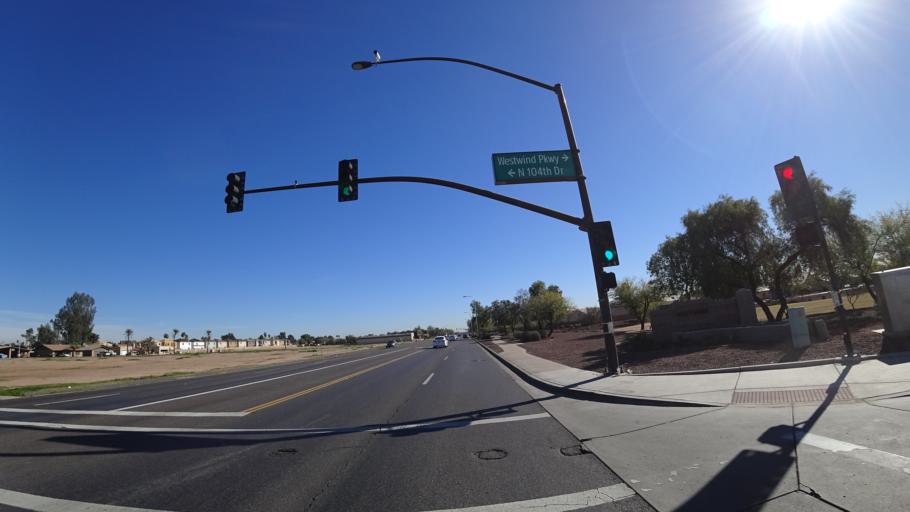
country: US
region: Arizona
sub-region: Maricopa County
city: Tolleson
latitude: 33.4936
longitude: -112.2851
